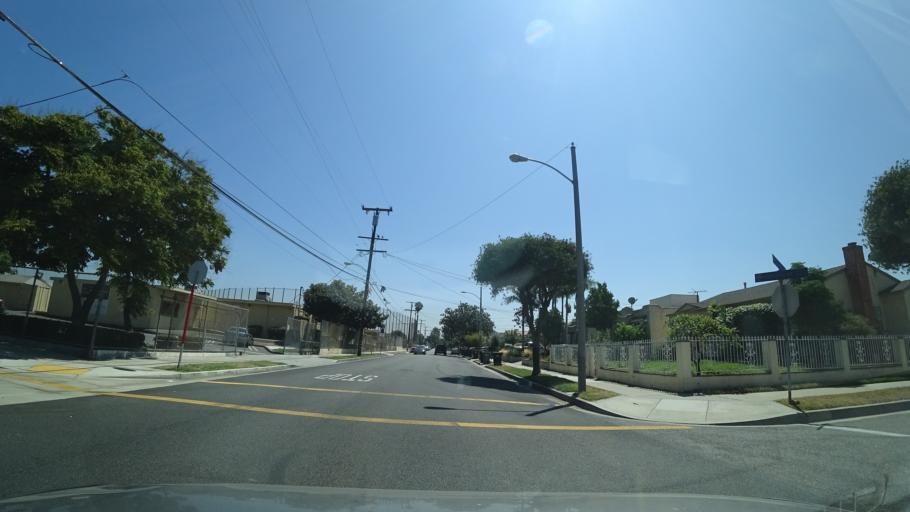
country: US
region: California
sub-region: Los Angeles County
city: Inglewood
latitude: 33.9565
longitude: -118.3638
